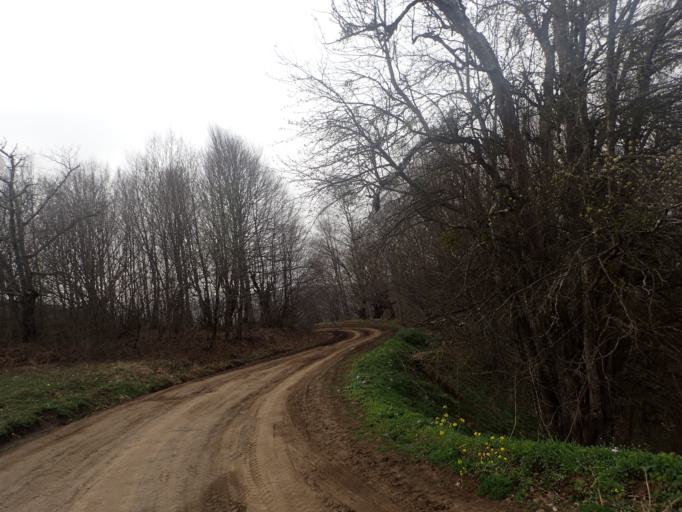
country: TR
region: Ordu
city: Kumru
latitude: 40.8234
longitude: 37.1529
